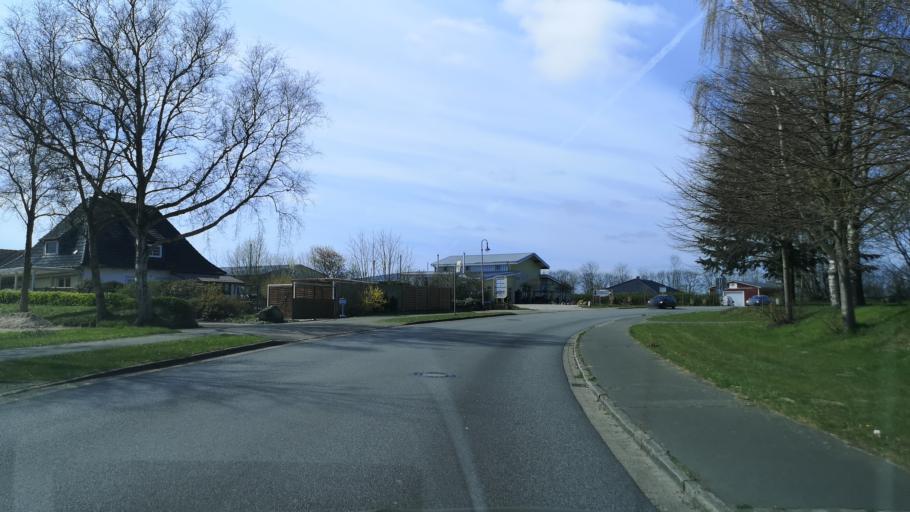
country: DE
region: Schleswig-Holstein
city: Hamdorf
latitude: 54.2270
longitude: 9.5132
